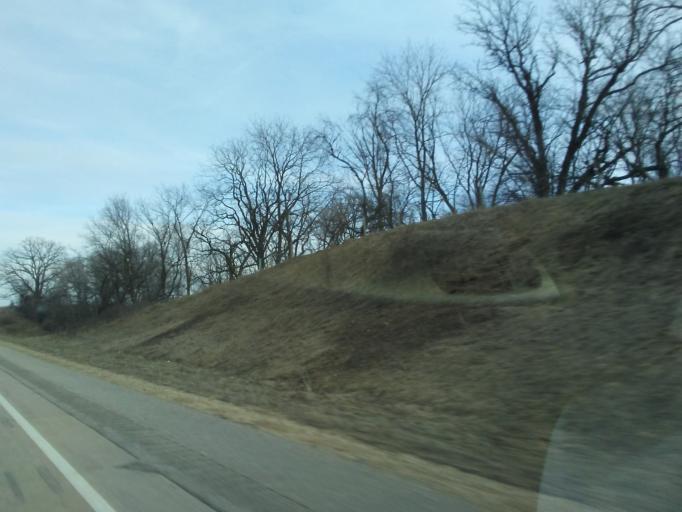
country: US
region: Wisconsin
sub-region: Iowa County
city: Barneveld
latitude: 43.0099
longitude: -89.8743
